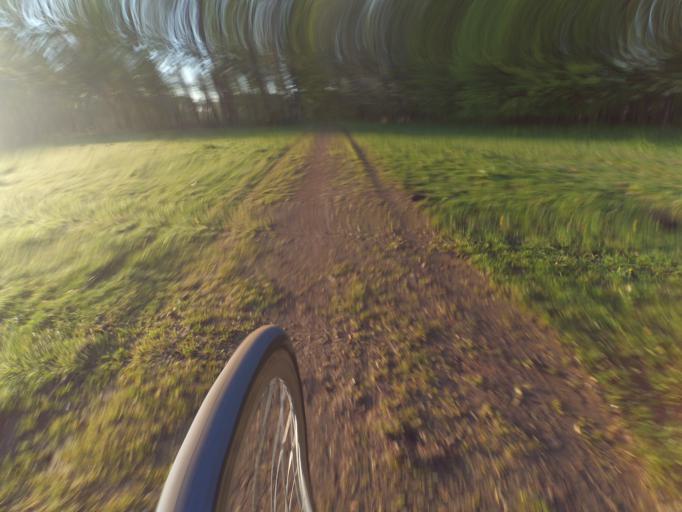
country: NL
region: Flevoland
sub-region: Gemeente Lelystad
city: Lelystad
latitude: 52.4186
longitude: 5.4927
